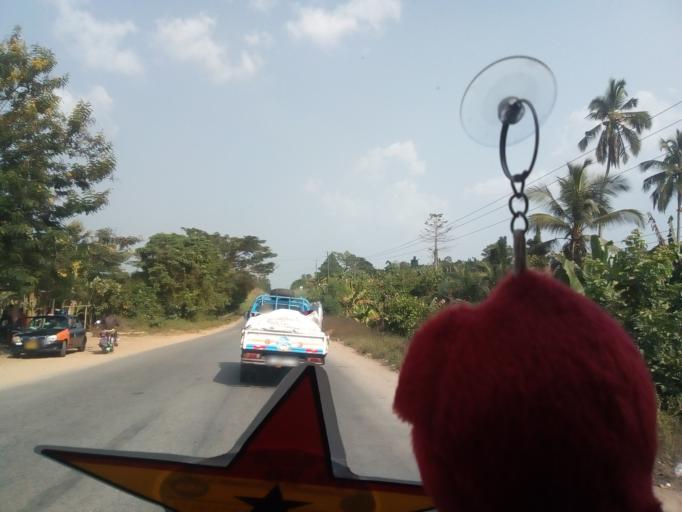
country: GH
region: Eastern
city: Suhum
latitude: 6.0440
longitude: -0.4244
